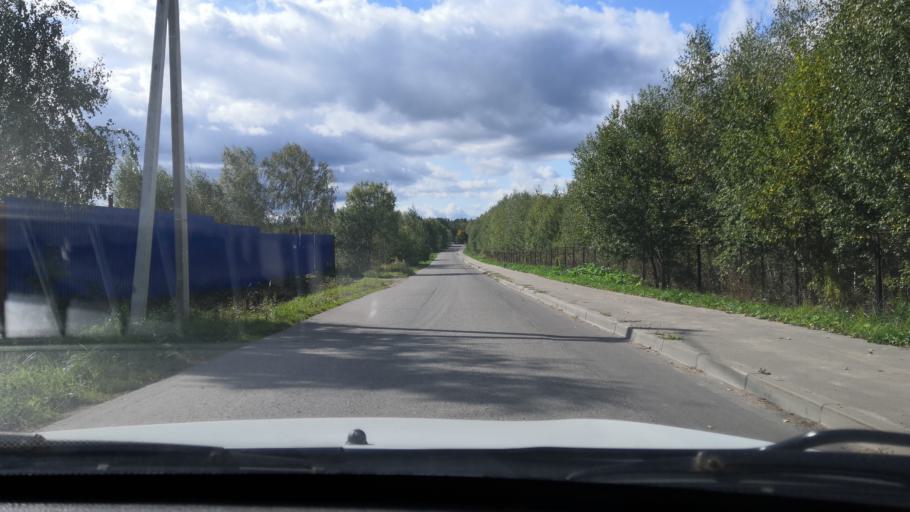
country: RU
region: Moskovskaya
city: Povarovo
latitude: 56.0669
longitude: 37.0470
